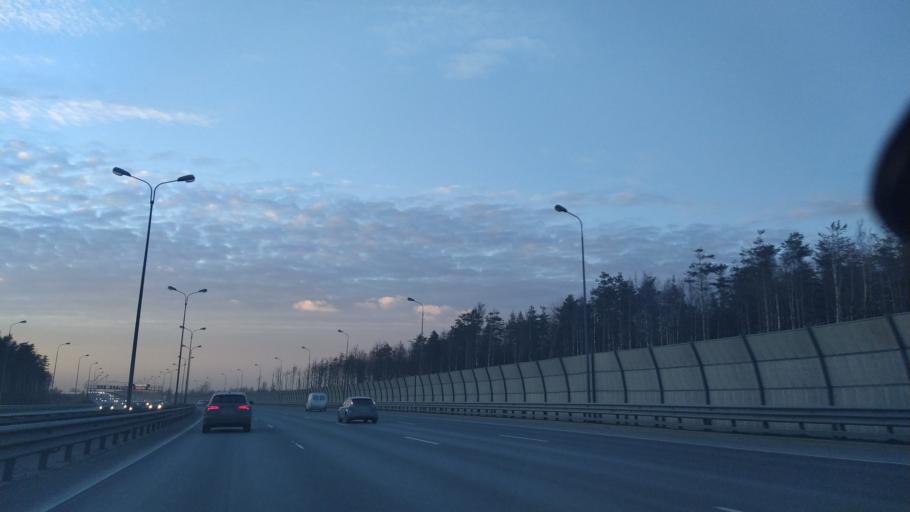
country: RU
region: St.-Petersburg
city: Krasnogvargeisky
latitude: 59.9726
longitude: 30.5459
